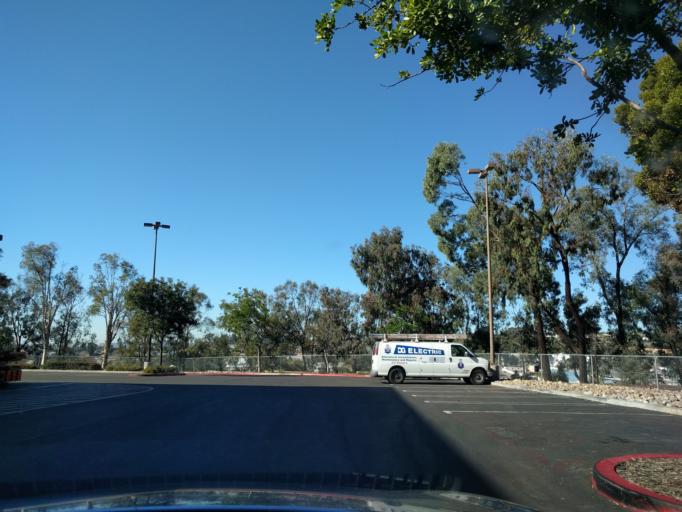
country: US
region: California
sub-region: San Diego County
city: National City
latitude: 32.7133
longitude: -117.1171
